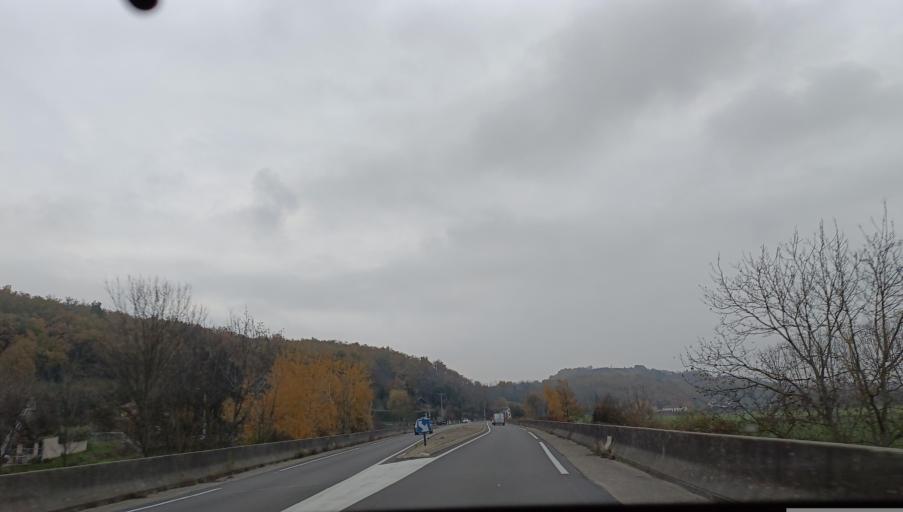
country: FR
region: Rhone-Alpes
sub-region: Departement de l'Isere
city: Serpaize
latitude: 45.5457
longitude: 4.9279
